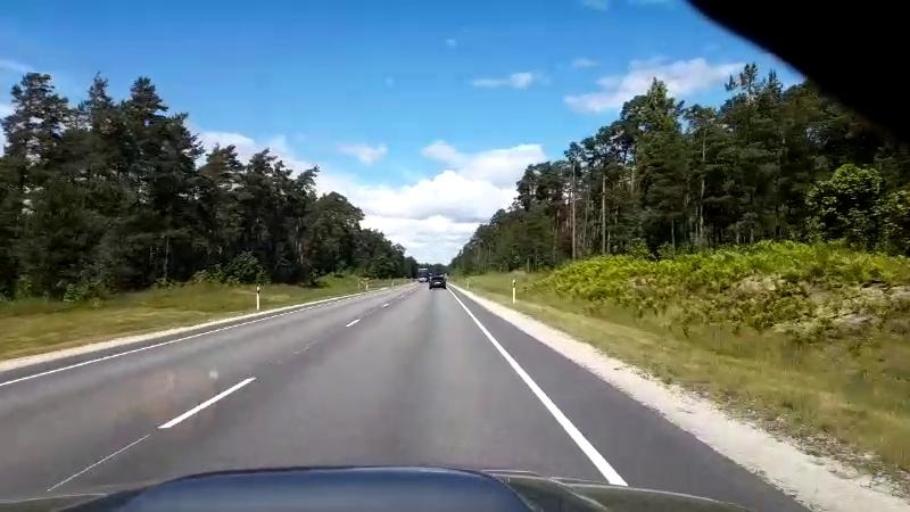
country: EE
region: Paernumaa
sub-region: Paernu linn
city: Parnu
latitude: 58.1949
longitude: 24.4886
